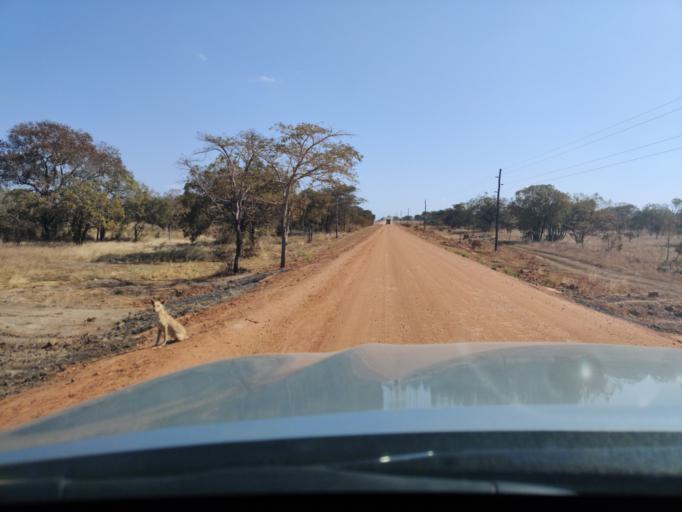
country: ZM
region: Central
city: Mkushi
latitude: -13.9902
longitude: 29.5333
